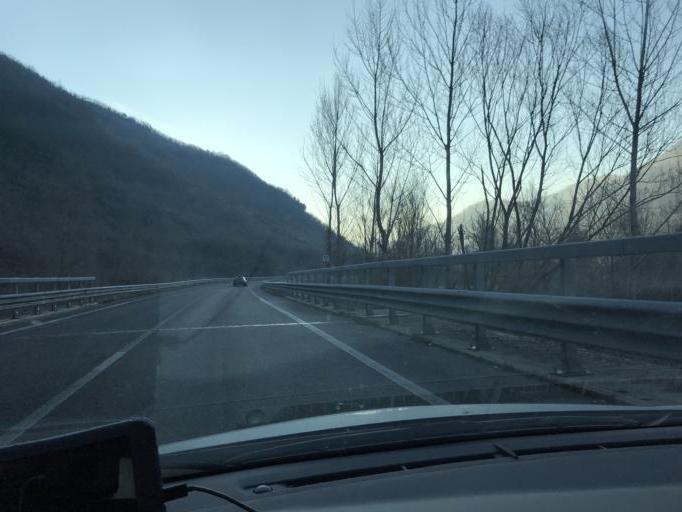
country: IT
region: Latium
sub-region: Provincia di Rieti
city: Concerviano
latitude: 42.3436
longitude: 12.9687
